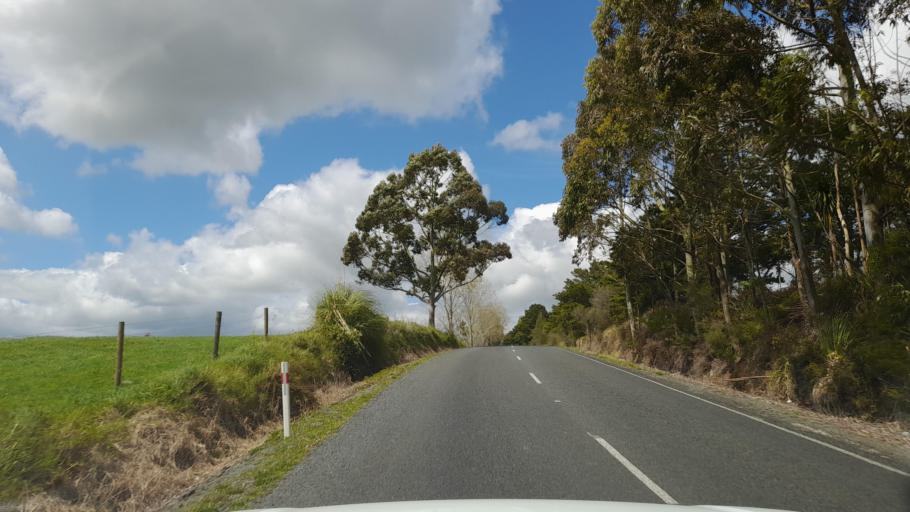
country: NZ
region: Northland
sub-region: Whangarei
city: Maungatapere
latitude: -35.6271
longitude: 174.0940
